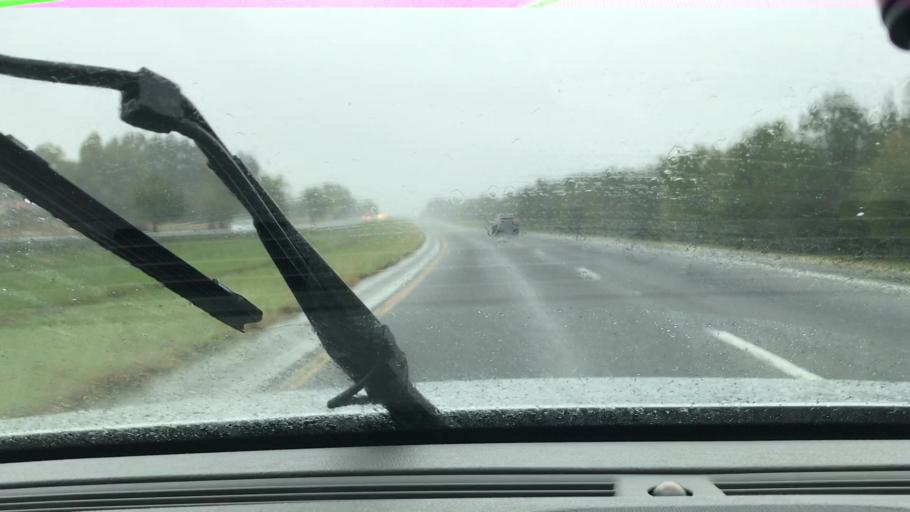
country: US
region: Alabama
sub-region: Limestone County
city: Ardmore
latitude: 34.9347
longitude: -86.8969
